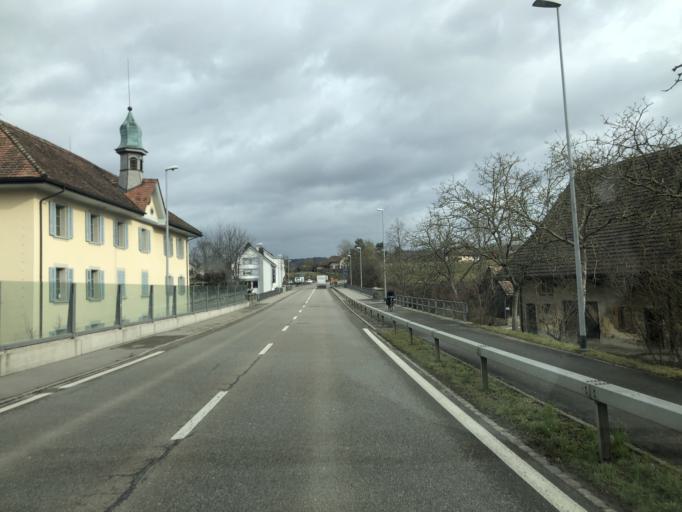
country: CH
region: Aargau
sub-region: Bezirk Brugg
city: Windisch
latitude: 47.4769
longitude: 8.2266
